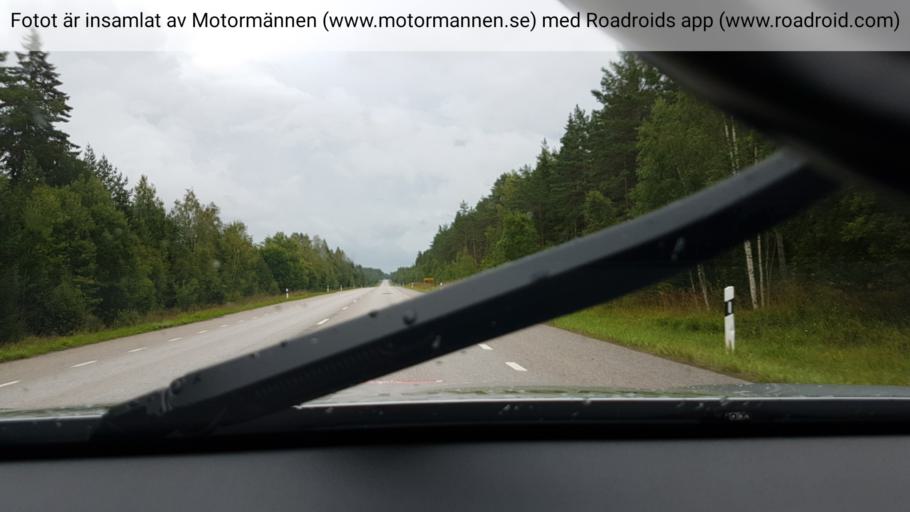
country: SE
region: Uppsala
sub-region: Alvkarleby Kommun
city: AElvkarleby
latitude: 60.5532
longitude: 17.4889
